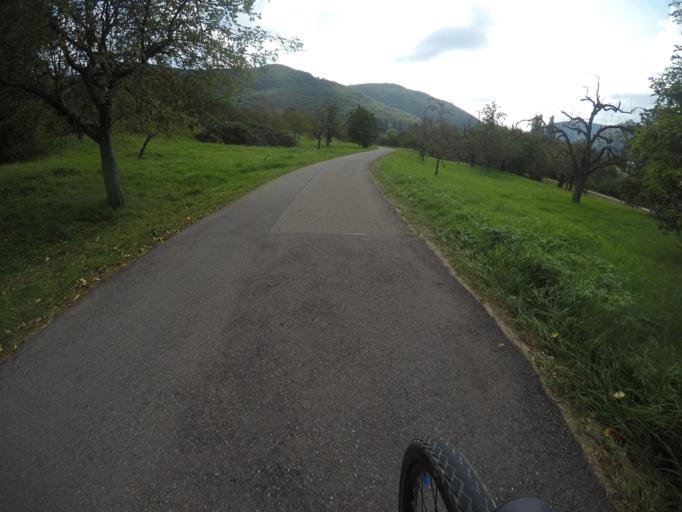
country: DE
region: Baden-Wuerttemberg
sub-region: Tuebingen Region
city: Dettingen an der Erms
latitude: 48.5146
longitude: 9.3668
